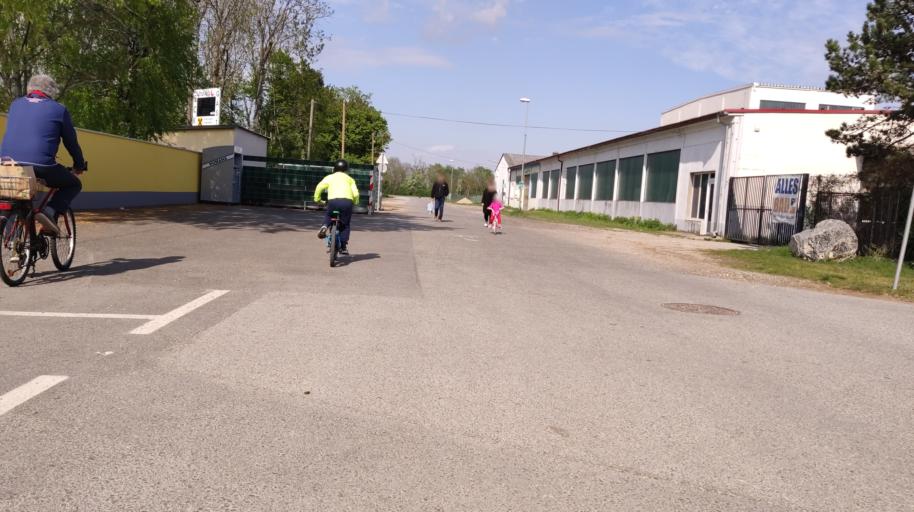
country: AT
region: Burgenland
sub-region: Politischer Bezirk Neusiedl am See
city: Kittsee
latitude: 48.0959
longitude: 17.0621
